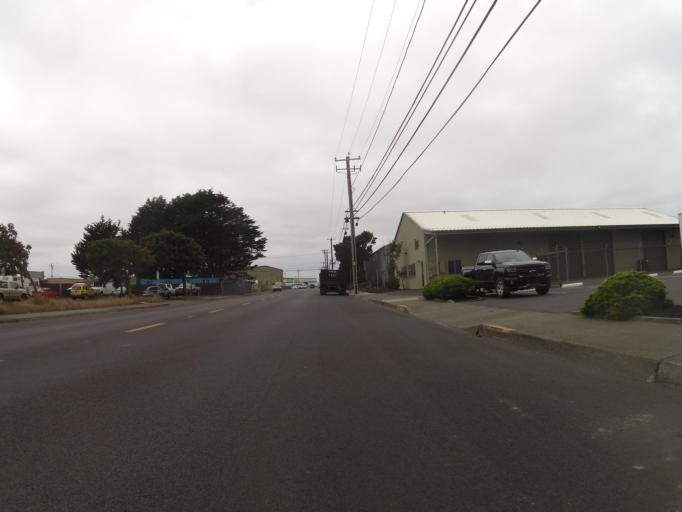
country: US
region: California
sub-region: Humboldt County
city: Eureka
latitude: 40.7982
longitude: -124.1769
